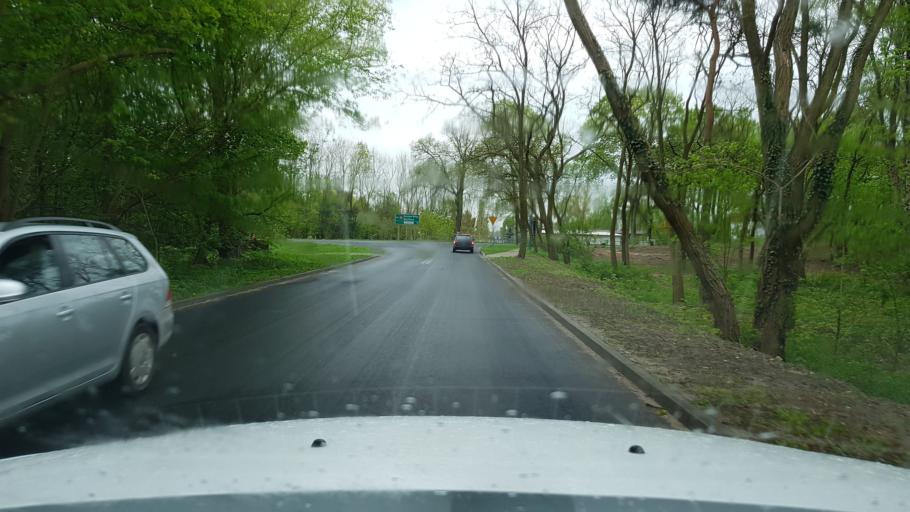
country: PL
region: West Pomeranian Voivodeship
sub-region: Powiat mysliborski
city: Debno
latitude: 52.7428
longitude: 14.7123
